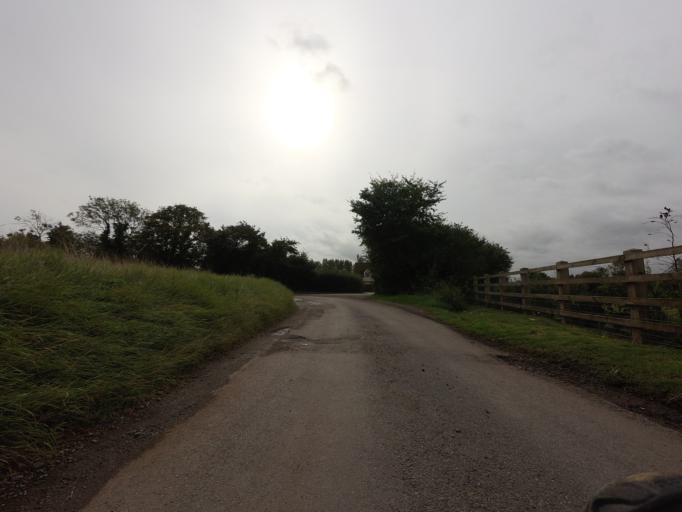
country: GB
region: England
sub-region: Hertfordshire
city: Reed
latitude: 51.9804
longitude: 0.0443
